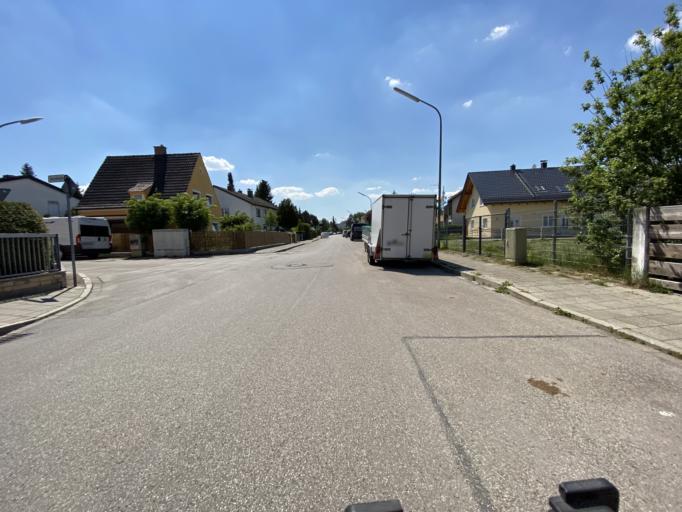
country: DE
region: Bavaria
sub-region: Upper Bavaria
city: Germering
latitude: 48.1300
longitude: 11.3823
